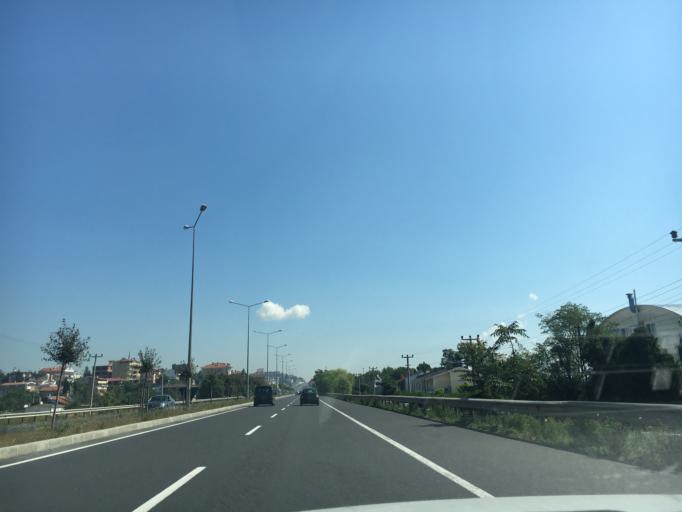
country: TR
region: Tekirdag
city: Sultankoy
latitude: 41.0142
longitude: 27.9850
